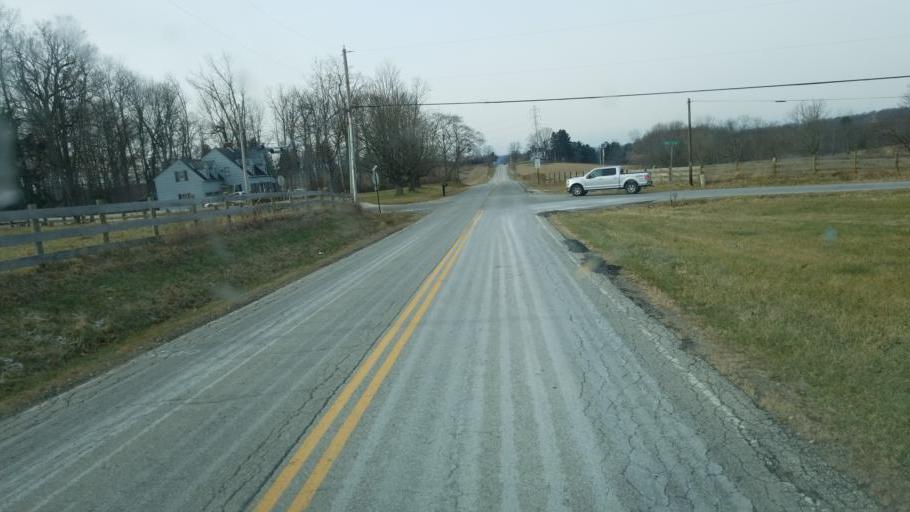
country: US
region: Ohio
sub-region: Richland County
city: Lexington
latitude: 40.6813
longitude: -82.5381
